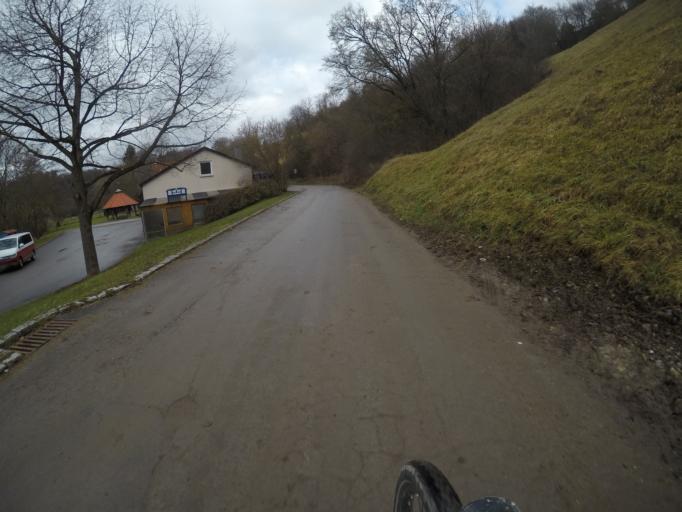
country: DE
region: Baden-Wuerttemberg
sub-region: Tuebingen Region
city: Rottenburg
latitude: 48.5454
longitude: 8.9185
